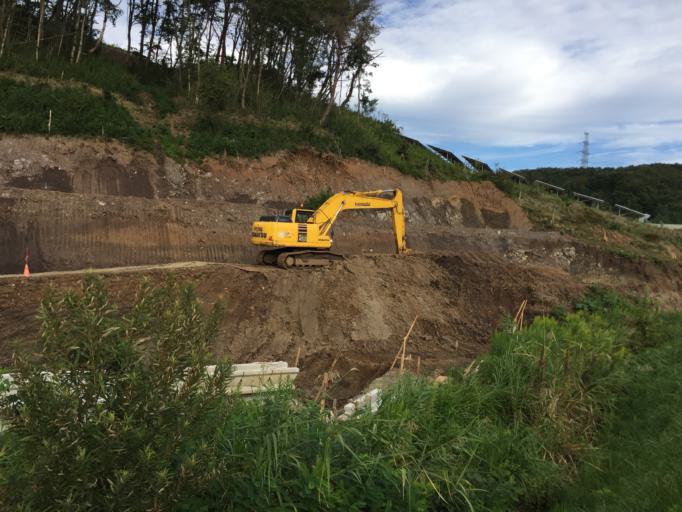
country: JP
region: Fukushima
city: Hobaramachi
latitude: 37.7915
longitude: 140.5171
